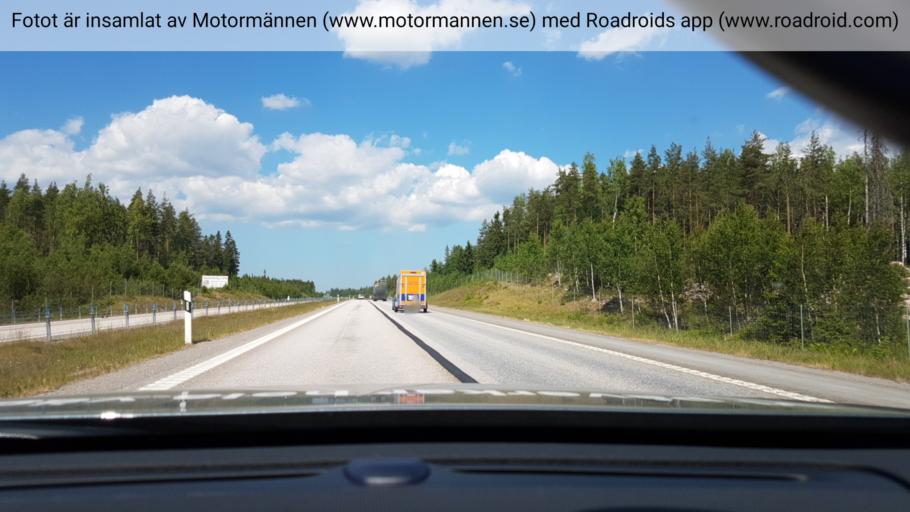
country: SE
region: Uppsala
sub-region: Tierps Kommun
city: Tierp
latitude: 60.2216
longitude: 17.4974
